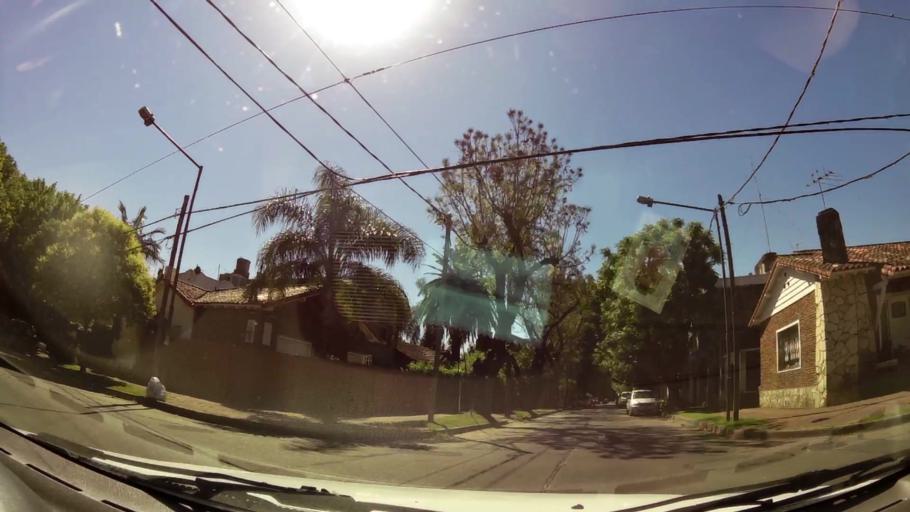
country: AR
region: Buenos Aires
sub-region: Partido de San Isidro
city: San Isidro
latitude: -34.4626
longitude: -58.5219
